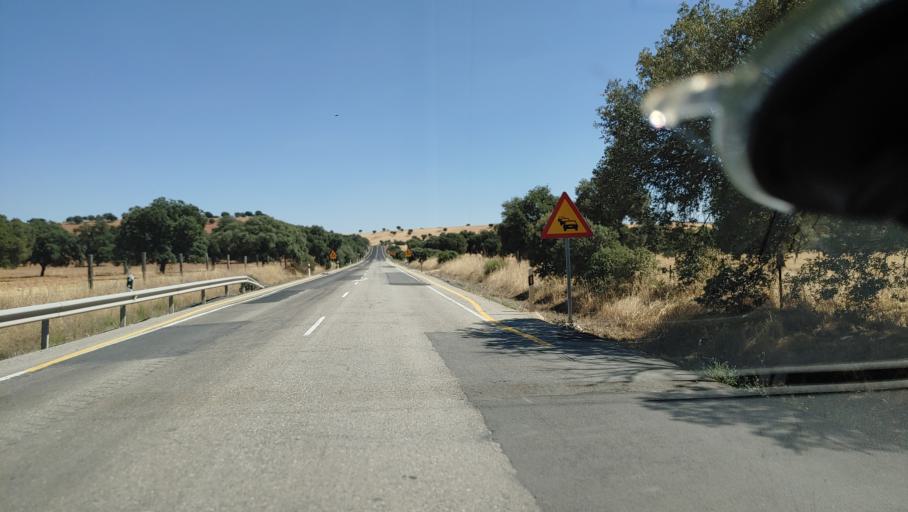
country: ES
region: Castille-La Mancha
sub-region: Provincia de Ciudad Real
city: Saceruela
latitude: 39.0160
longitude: -4.4724
